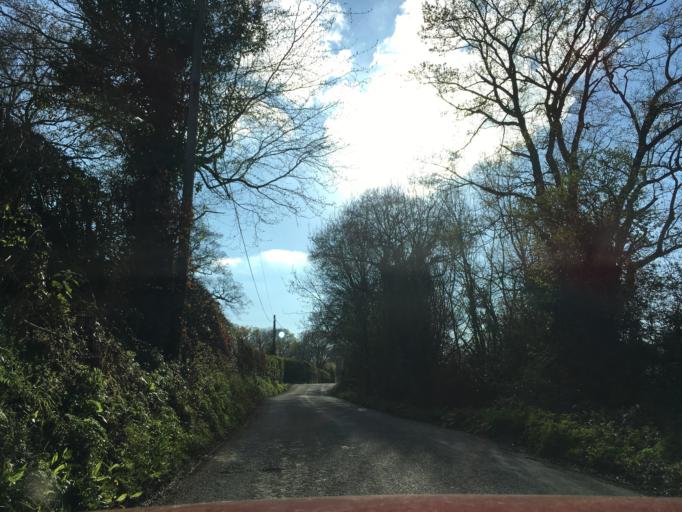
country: GB
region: Wales
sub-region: Torfaen County Borough
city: New Inn
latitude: 51.7059
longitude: -2.9724
